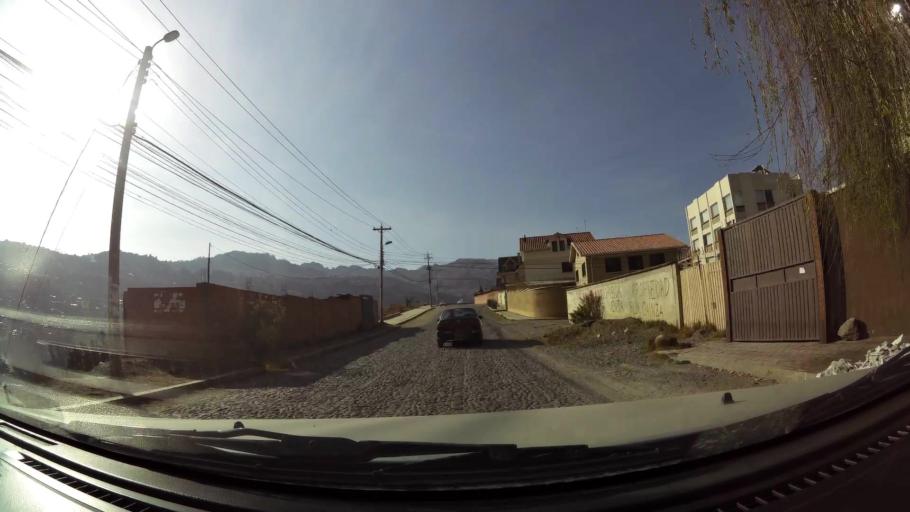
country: BO
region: La Paz
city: La Paz
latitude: -16.5109
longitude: -68.0841
